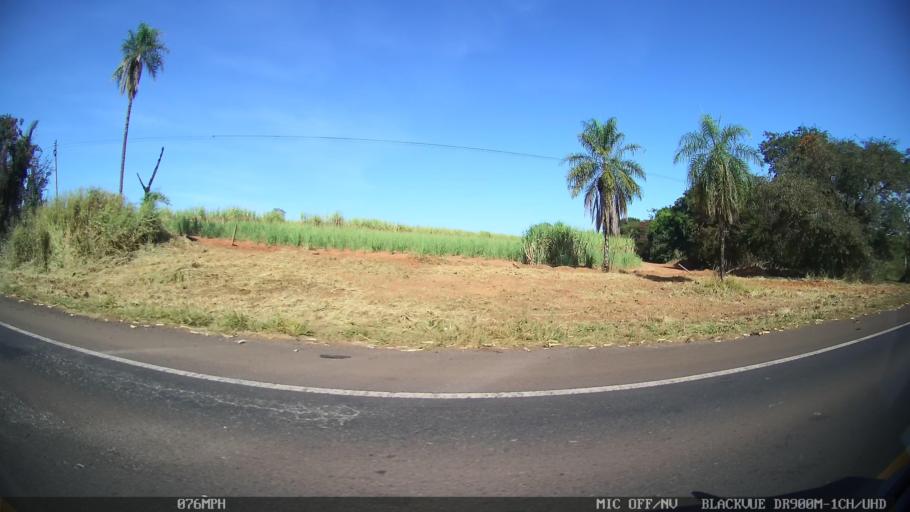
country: BR
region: Sao Paulo
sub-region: Barretos
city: Barretos
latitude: -20.5920
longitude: -48.7104
